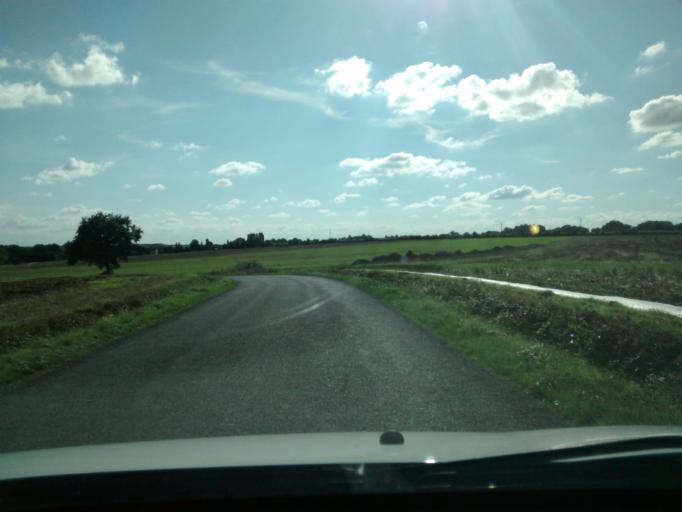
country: FR
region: Brittany
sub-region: Departement d'Ille-et-Vilaine
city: Cesson-Sevigne
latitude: 48.0957
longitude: -1.5825
